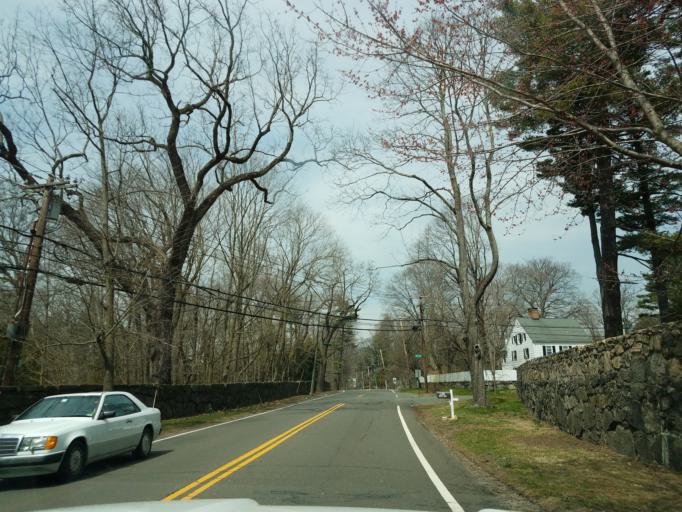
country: US
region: Connecticut
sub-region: Fairfield County
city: Greenwich
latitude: 41.0480
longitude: -73.6376
